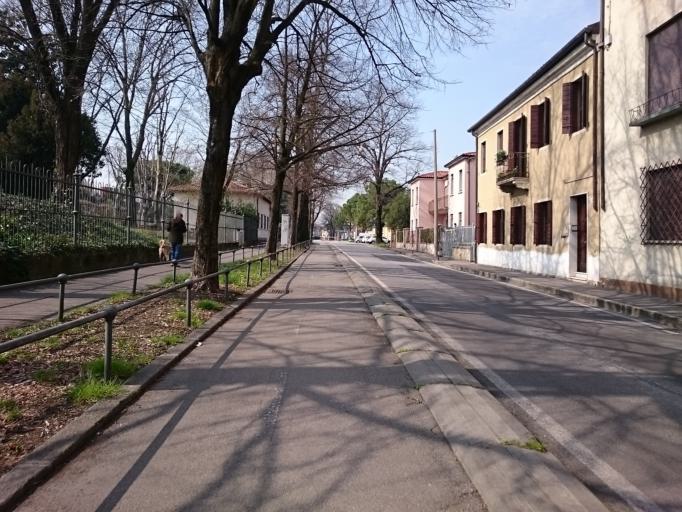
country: IT
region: Veneto
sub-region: Provincia di Padova
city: Padova
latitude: 45.3942
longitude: 11.8794
